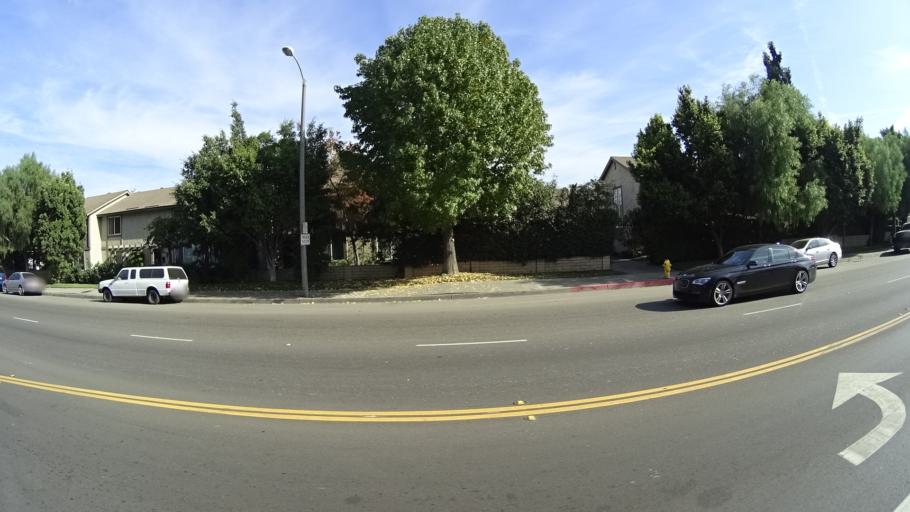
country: US
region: California
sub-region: Orange County
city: Stanton
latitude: 33.8000
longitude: -118.0111
